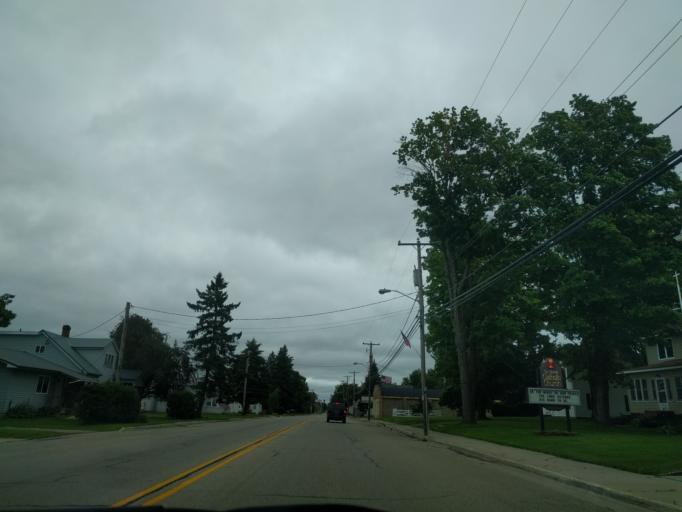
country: US
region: Michigan
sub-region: Delta County
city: Gladstone
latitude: 45.9781
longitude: -87.0740
